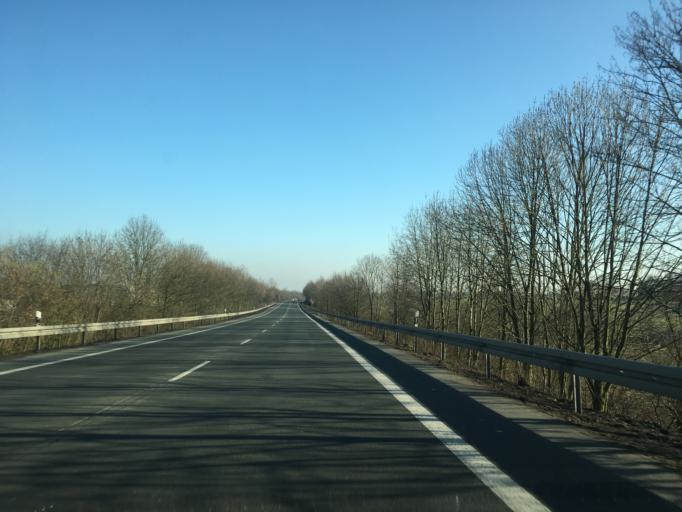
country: DE
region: North Rhine-Westphalia
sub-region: Regierungsbezirk Munster
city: Horstmar
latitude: 52.0744
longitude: 7.3020
